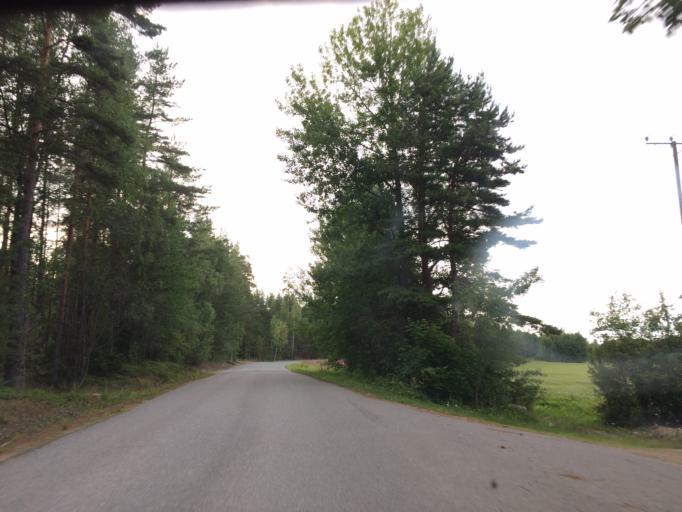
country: FI
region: Haeme
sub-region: Haemeenlinna
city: Tervakoski
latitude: 60.8403
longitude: 24.6269
